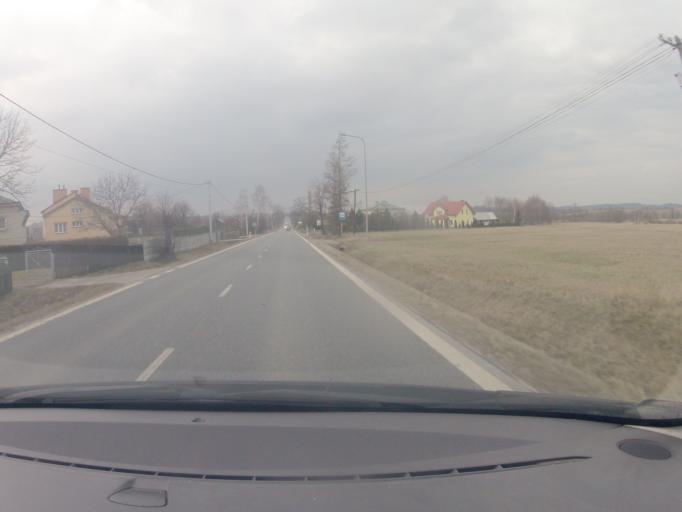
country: PL
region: Subcarpathian Voivodeship
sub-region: Powiat jasielski
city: Nowy Zmigrod
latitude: 49.5942
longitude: 21.5364
